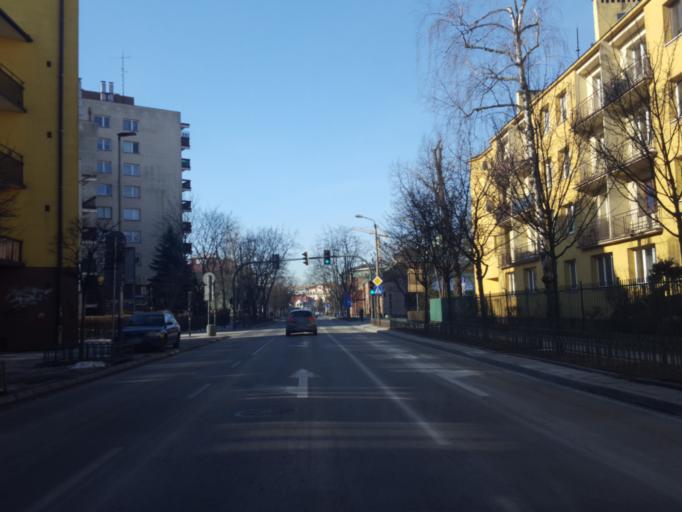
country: PL
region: Lesser Poland Voivodeship
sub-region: Krakow
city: Krakow
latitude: 50.0699
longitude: 19.9624
